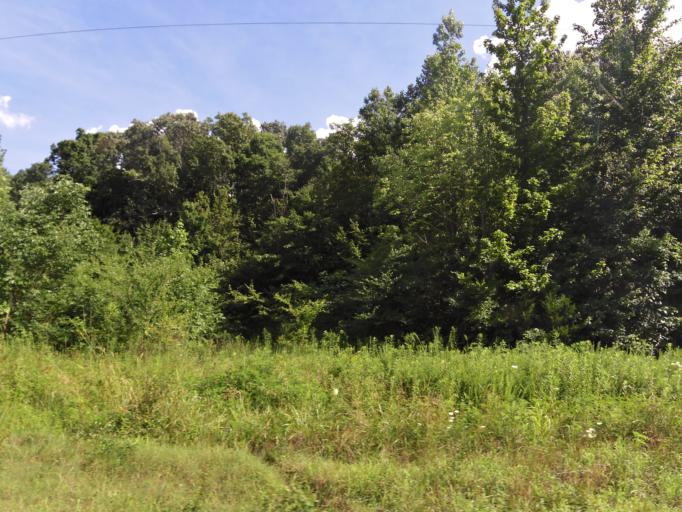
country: US
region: Tennessee
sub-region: Gibson County
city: Milan
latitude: 35.9727
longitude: -88.7153
